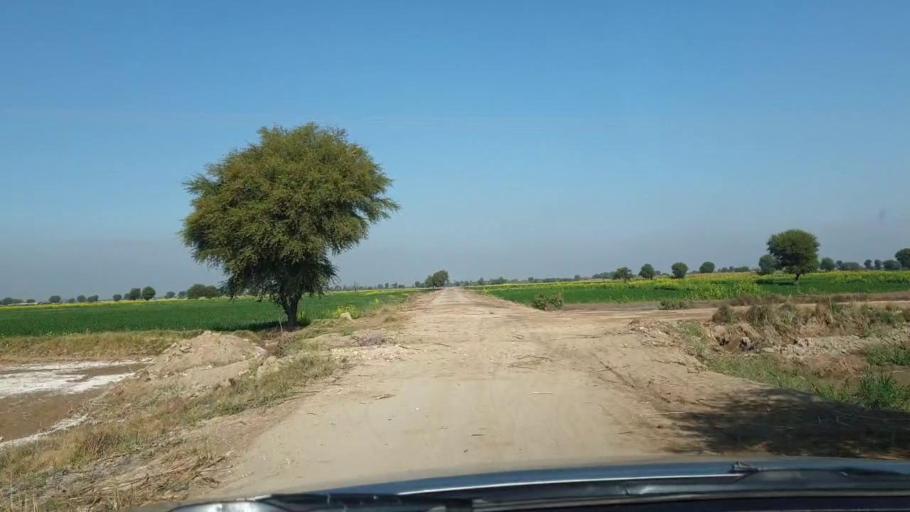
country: PK
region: Sindh
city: Jhol
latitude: 25.8920
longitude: 68.9054
